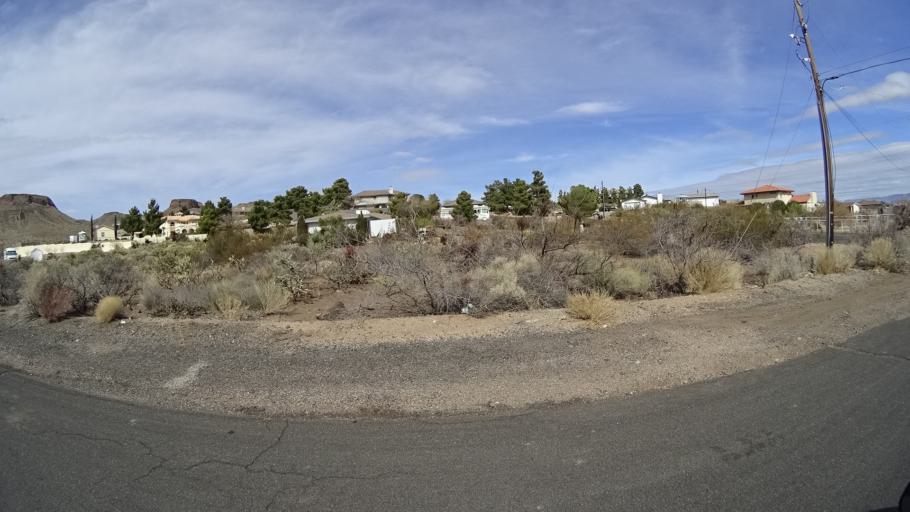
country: US
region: Arizona
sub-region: Mohave County
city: New Kingman-Butler
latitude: 35.2314
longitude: -114.0539
